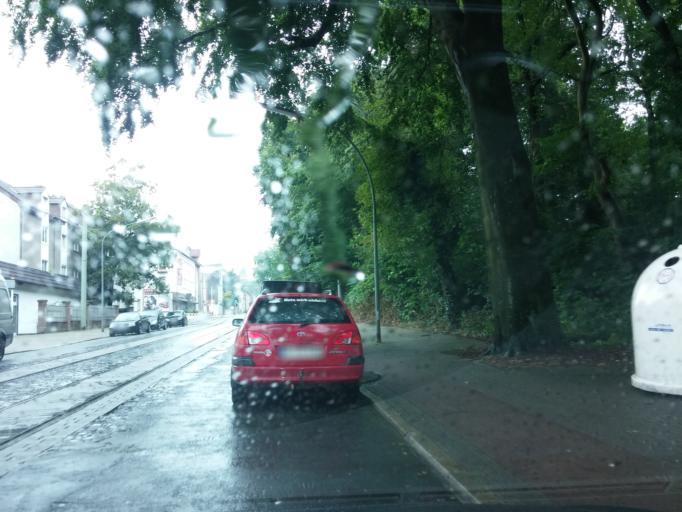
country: DE
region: North Rhine-Westphalia
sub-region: Regierungsbezirk Munster
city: Gladbeck
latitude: 51.5651
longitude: 7.0466
